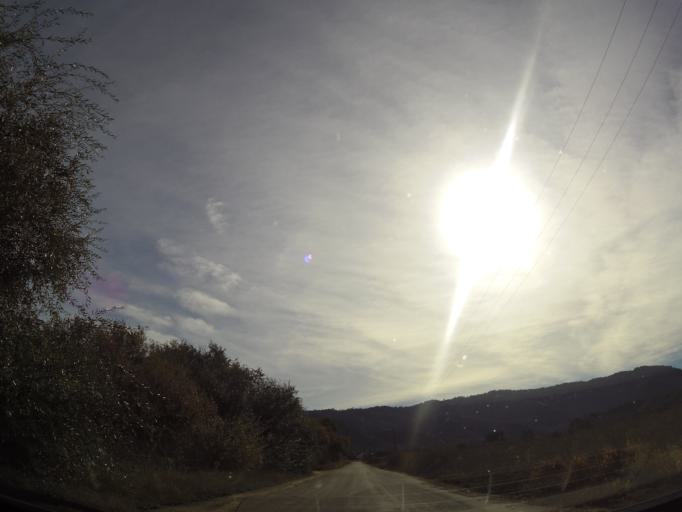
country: US
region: California
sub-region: San Benito County
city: Ridgemark
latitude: 36.7042
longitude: -121.3290
